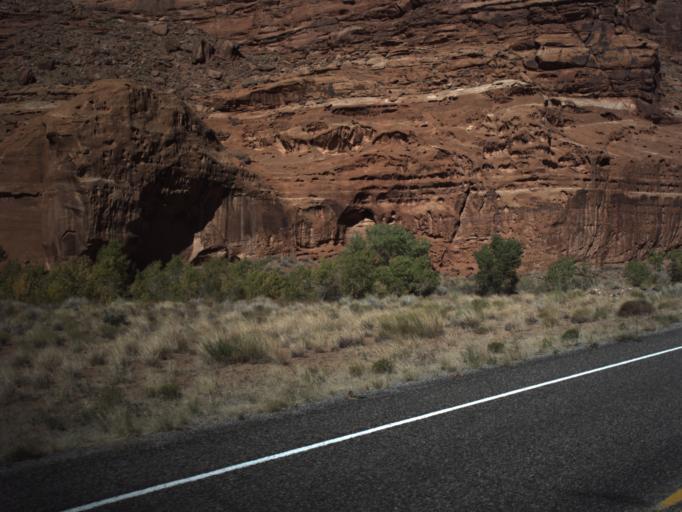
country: US
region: Utah
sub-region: San Juan County
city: Blanding
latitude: 37.9781
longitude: -110.4922
